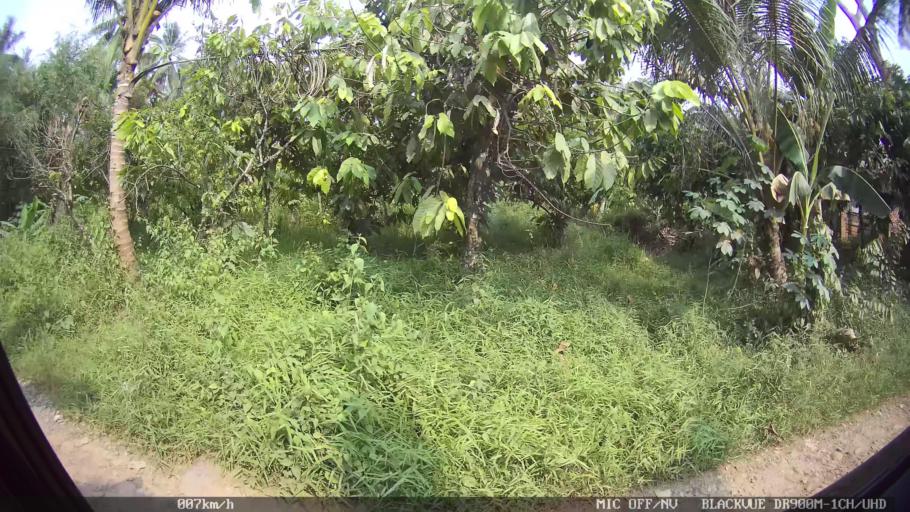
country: ID
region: Lampung
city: Gadingrejo
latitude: -5.3952
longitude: 105.0235
